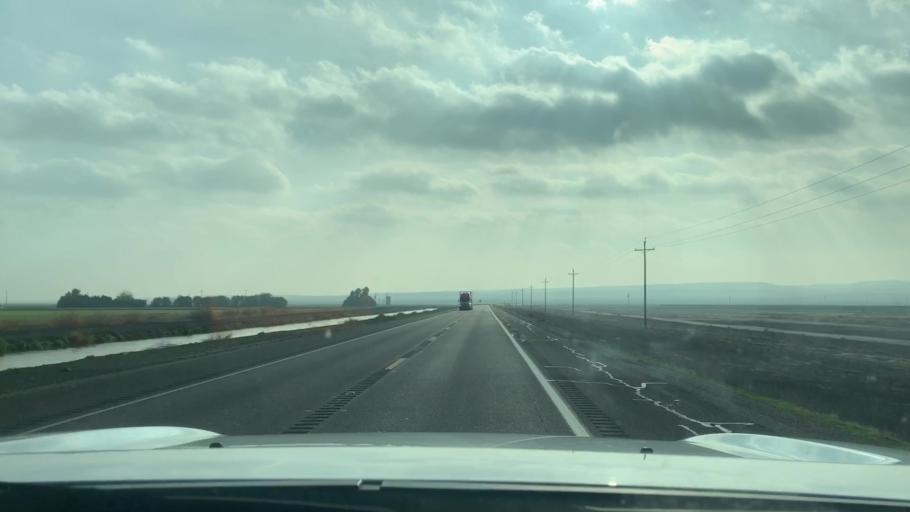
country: US
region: California
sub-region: Kings County
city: Kettleman City
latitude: 36.0555
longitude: -119.9423
